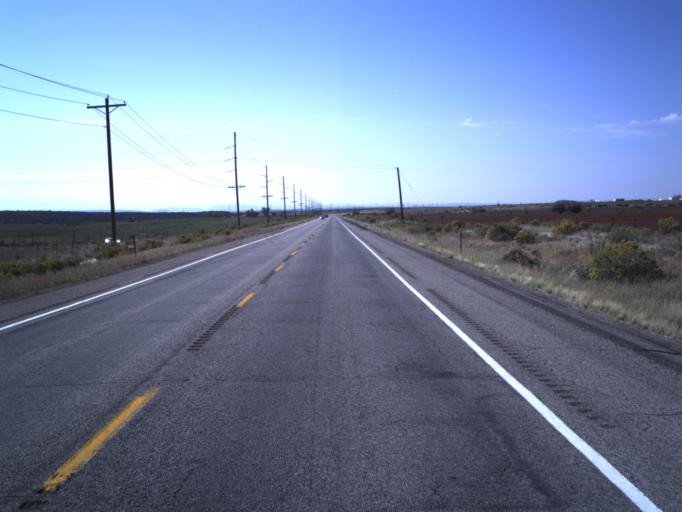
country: US
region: Utah
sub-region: San Juan County
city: Blanding
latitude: 37.5640
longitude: -109.4895
